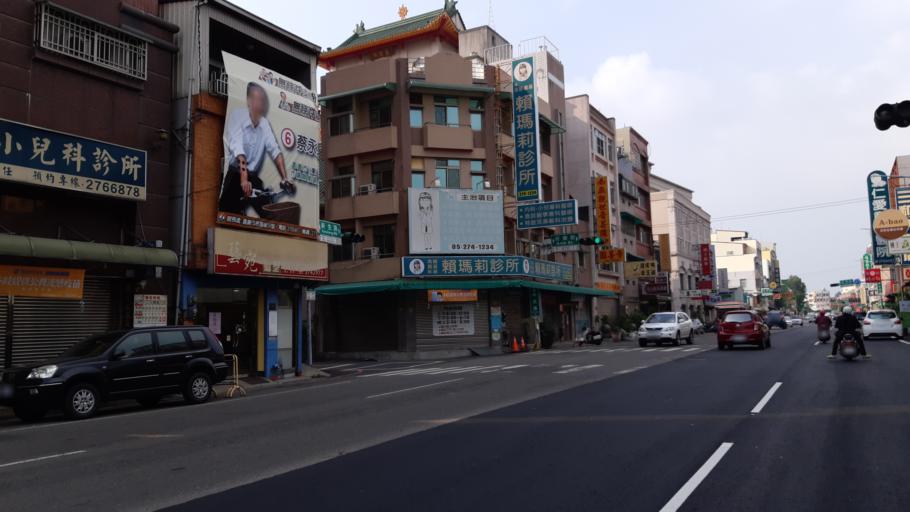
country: TW
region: Taiwan
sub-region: Chiayi
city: Jiayi Shi
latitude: 23.4830
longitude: 120.4611
